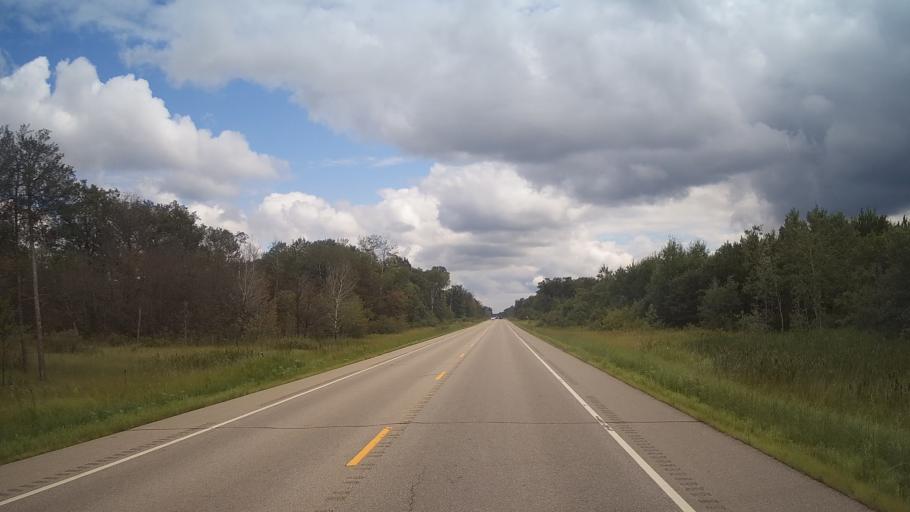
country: US
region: Wisconsin
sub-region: Adams County
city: Friendship
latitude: 44.0253
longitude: -89.7370
